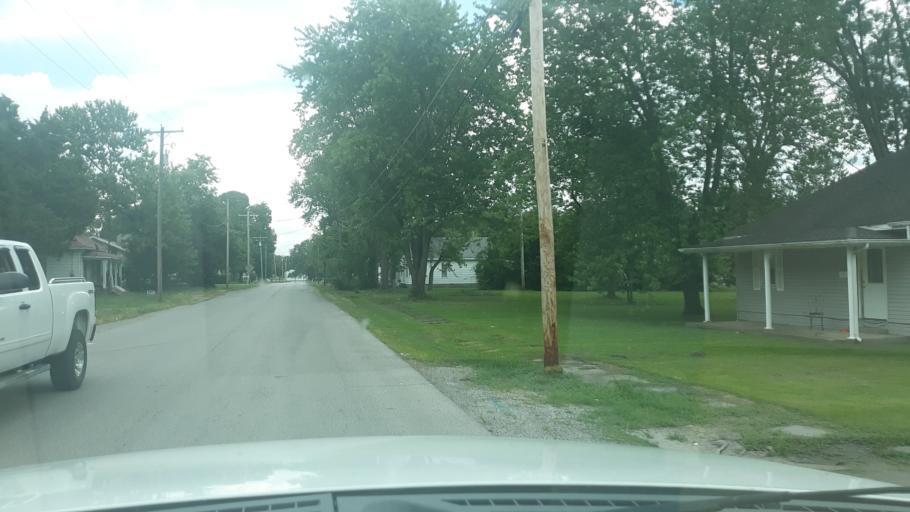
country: US
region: Illinois
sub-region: Saline County
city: Eldorado
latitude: 37.8073
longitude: -88.4564
